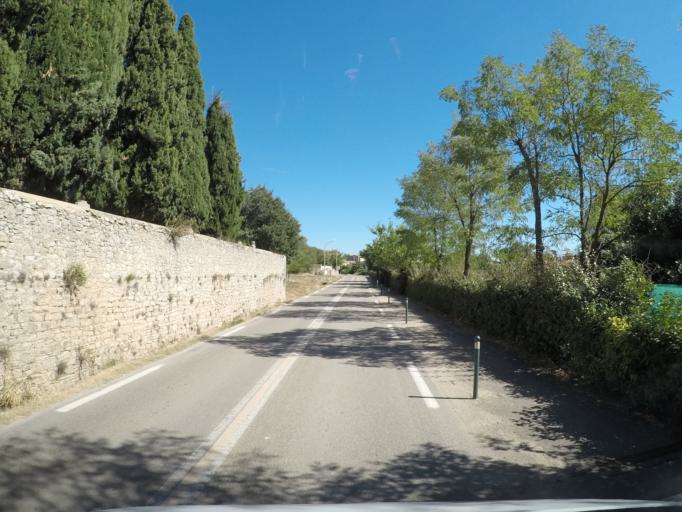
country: FR
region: Languedoc-Roussillon
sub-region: Departement de l'Herault
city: Saint-Martin-de-Londres
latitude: 43.7419
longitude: 3.7002
